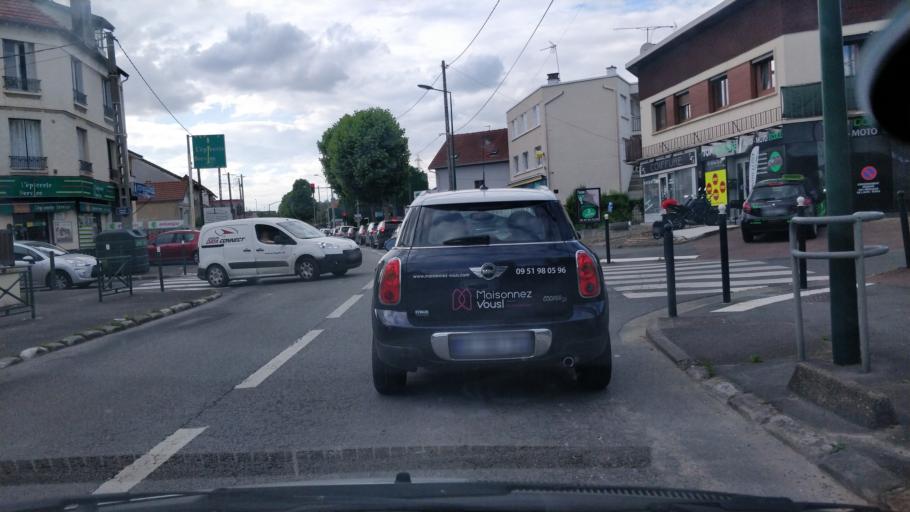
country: FR
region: Ile-de-France
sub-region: Departement de Seine-Saint-Denis
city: Neuilly-sur-Marne
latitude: 48.8736
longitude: 2.5530
